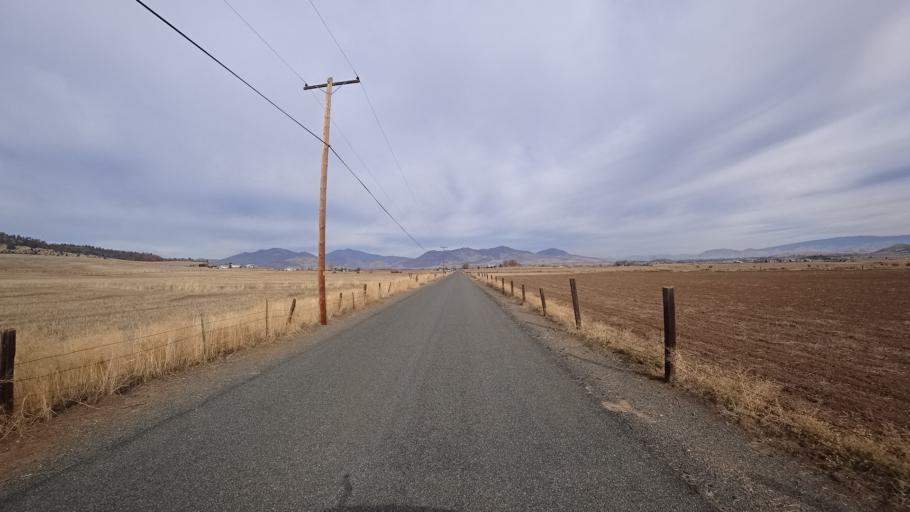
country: US
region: California
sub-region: Siskiyou County
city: Montague
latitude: 41.6970
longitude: -122.5639
